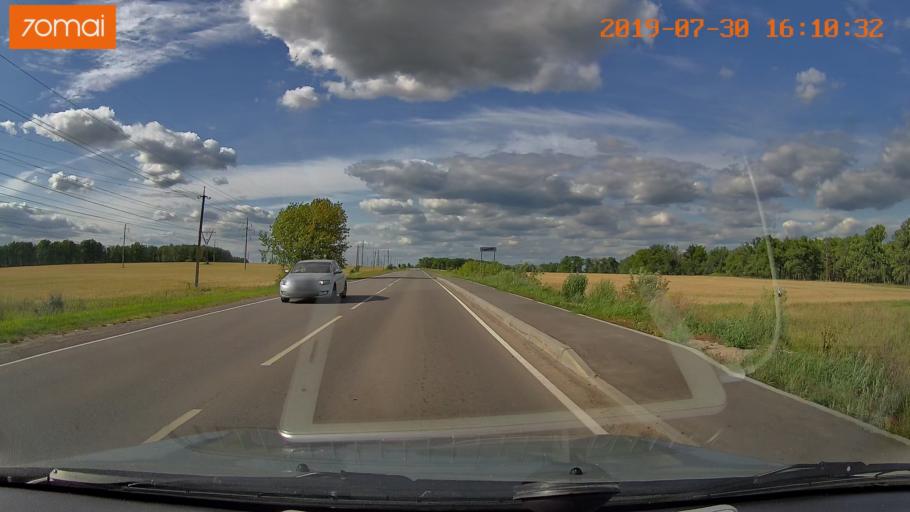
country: RU
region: Moskovskaya
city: Peski
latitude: 55.2635
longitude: 38.7155
